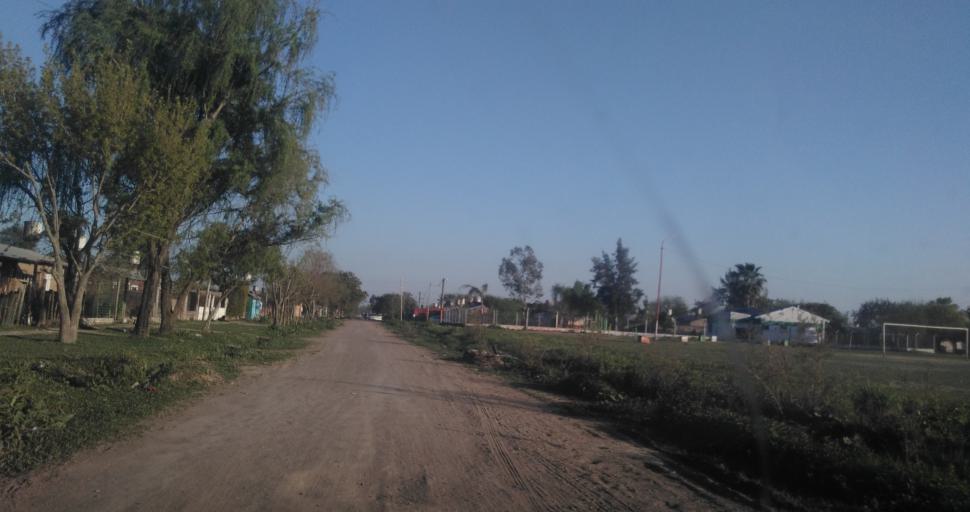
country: AR
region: Chaco
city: Resistencia
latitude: -27.4807
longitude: -59.0054
